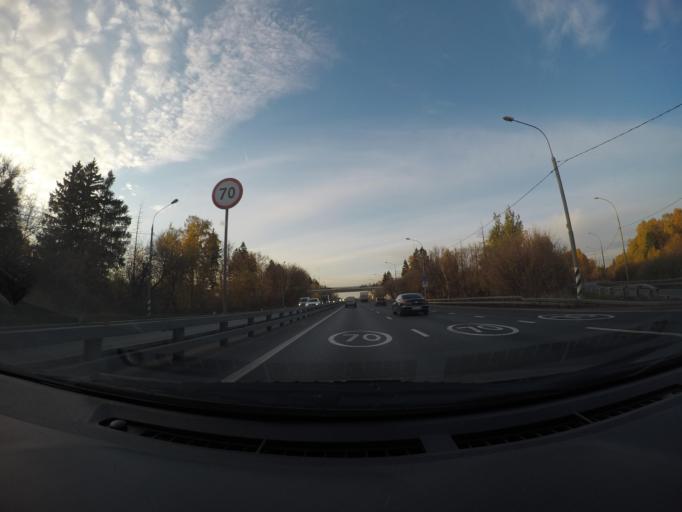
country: RU
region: Moskovskaya
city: Skhodnya
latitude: 55.9689
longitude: 37.3230
